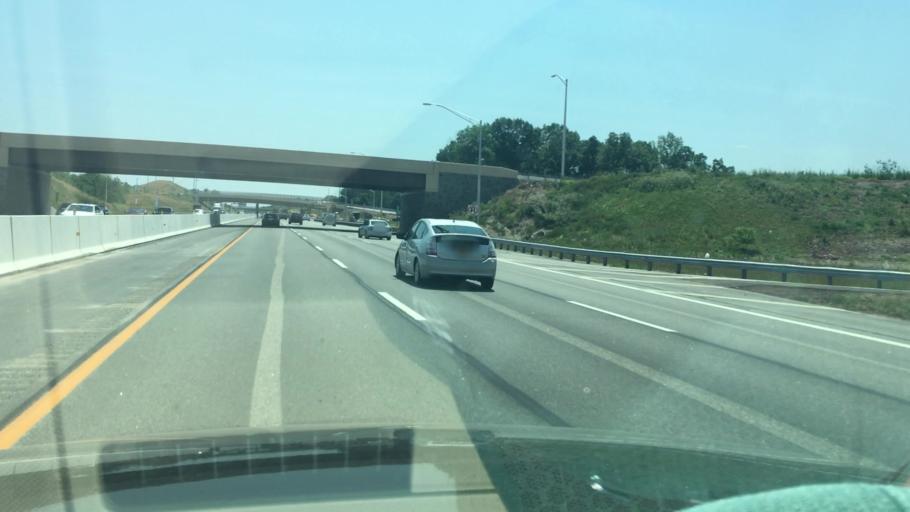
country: US
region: Pennsylvania
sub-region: Montgomery County
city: Kulpsville
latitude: 40.2523
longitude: -75.3479
